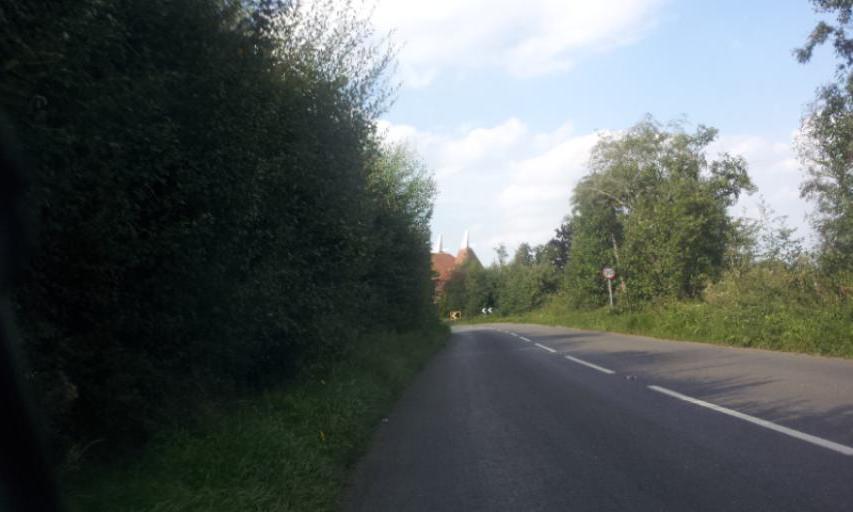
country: GB
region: England
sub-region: Kent
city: Marden
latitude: 51.1887
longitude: 0.4547
